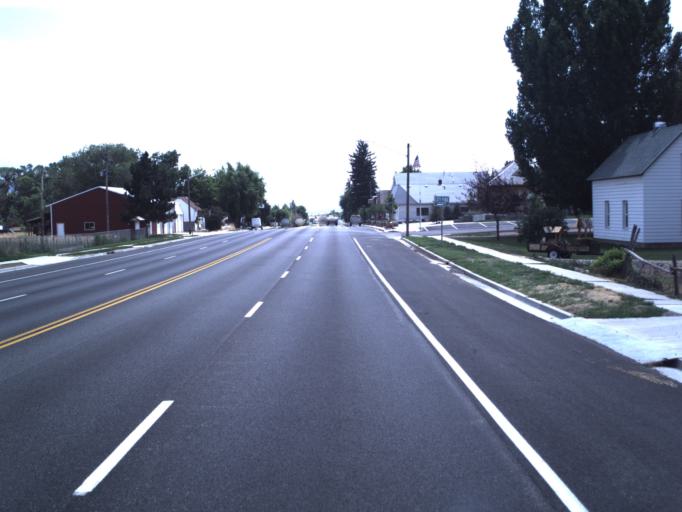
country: US
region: Utah
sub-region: Sanpete County
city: Fountain Green
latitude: 39.6291
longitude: -111.6345
